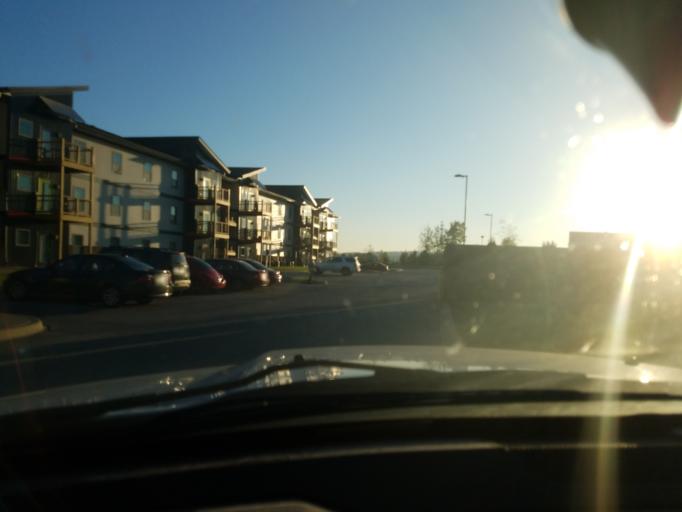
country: US
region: Indiana
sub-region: Floyd County
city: New Albany
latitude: 38.3394
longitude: -85.8142
